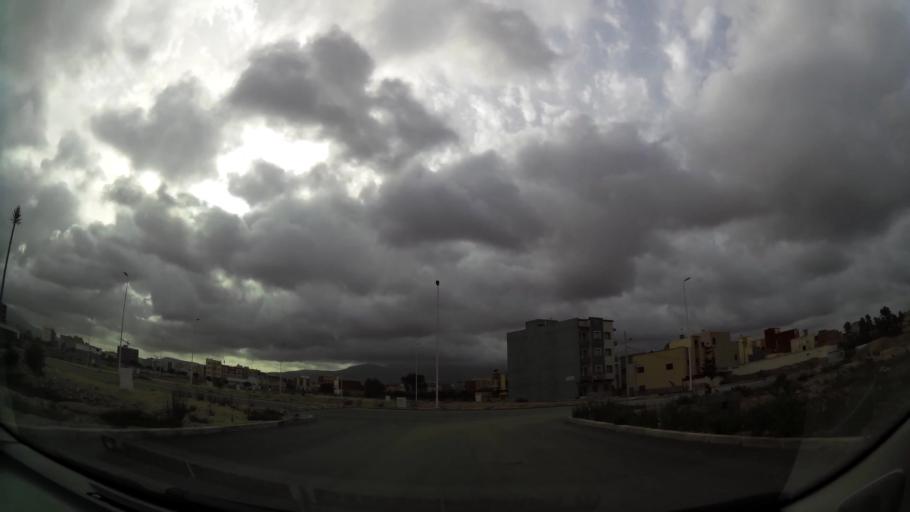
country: MA
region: Oriental
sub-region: Nador
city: Nador
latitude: 35.1548
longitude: -2.9137
